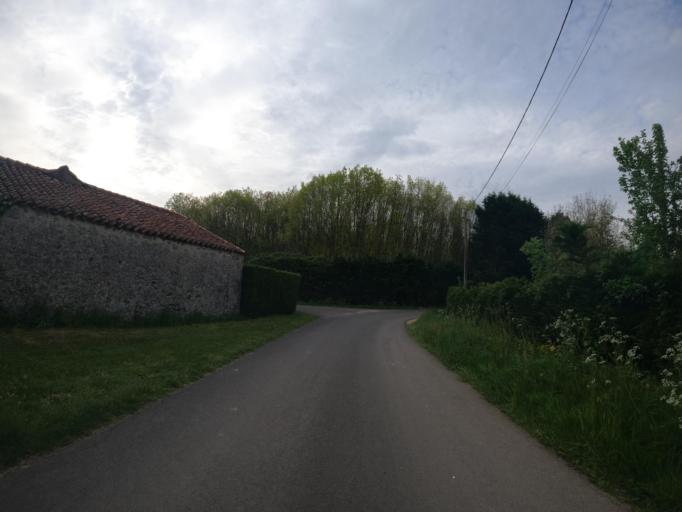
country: FR
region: Poitou-Charentes
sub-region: Departement des Deux-Sevres
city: La Chapelle-Saint-Laurent
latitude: 46.6976
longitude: -0.4895
